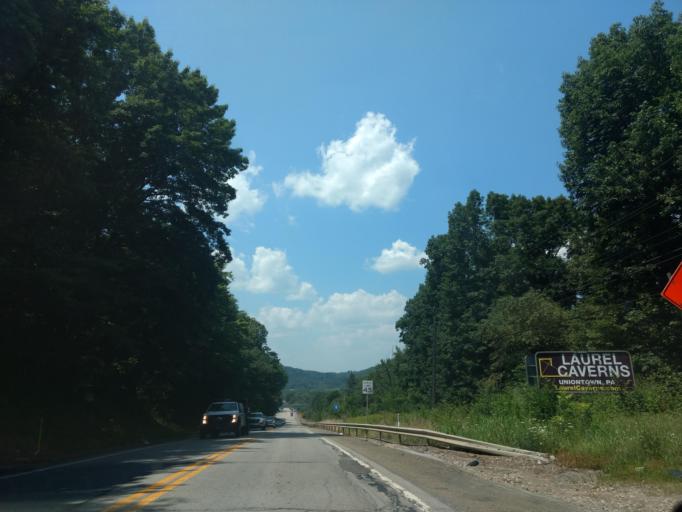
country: US
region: Pennsylvania
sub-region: Butler County
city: Zelienople
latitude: 40.7994
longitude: -80.1107
